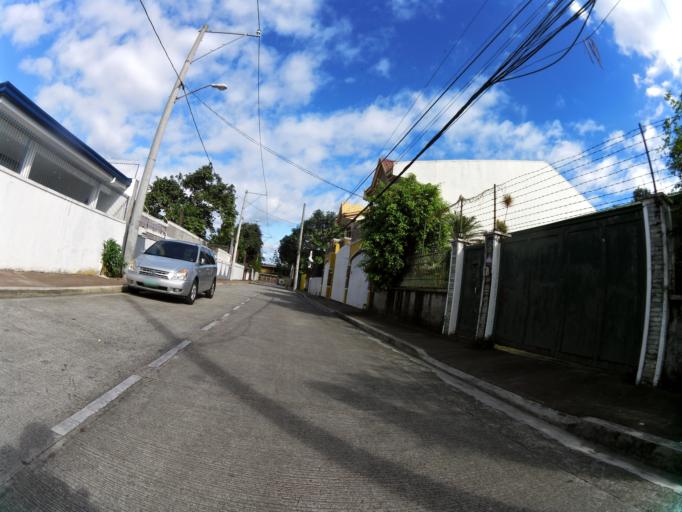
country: PH
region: Metro Manila
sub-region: Marikina
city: Calumpang
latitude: 14.6267
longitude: 121.1005
